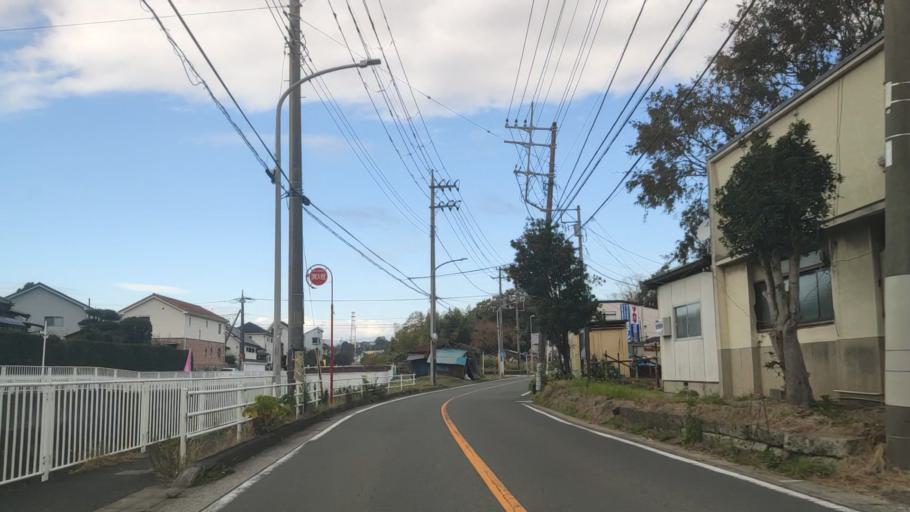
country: JP
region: Kanagawa
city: Minami-rinkan
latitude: 35.4273
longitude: 139.5209
